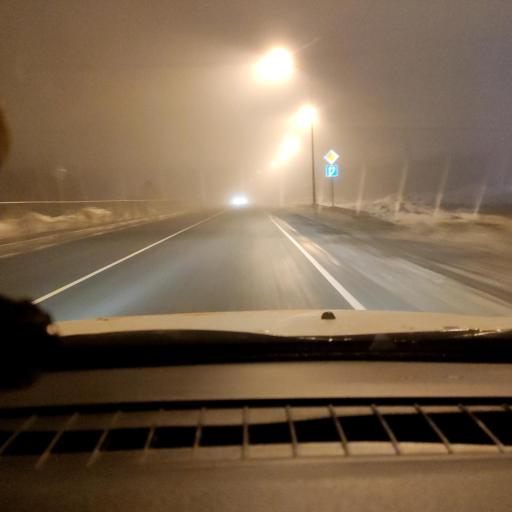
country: RU
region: Samara
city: Dubovyy Umet
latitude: 52.9705
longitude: 50.2784
